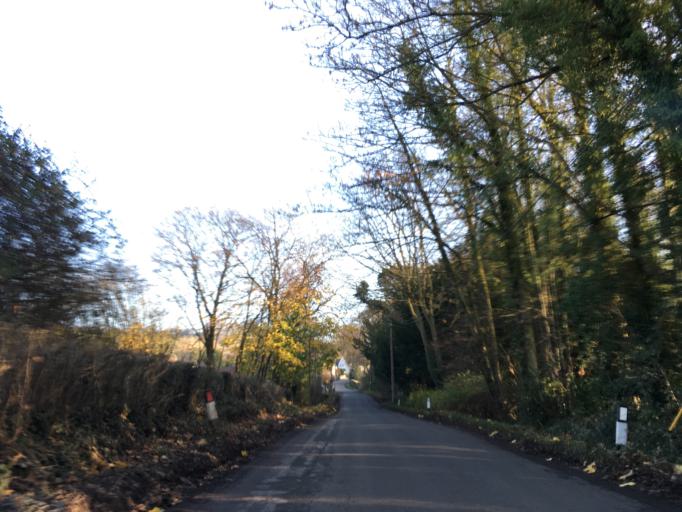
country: GB
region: England
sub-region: South Gloucestershire
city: Horton
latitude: 51.5588
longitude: -2.3510
